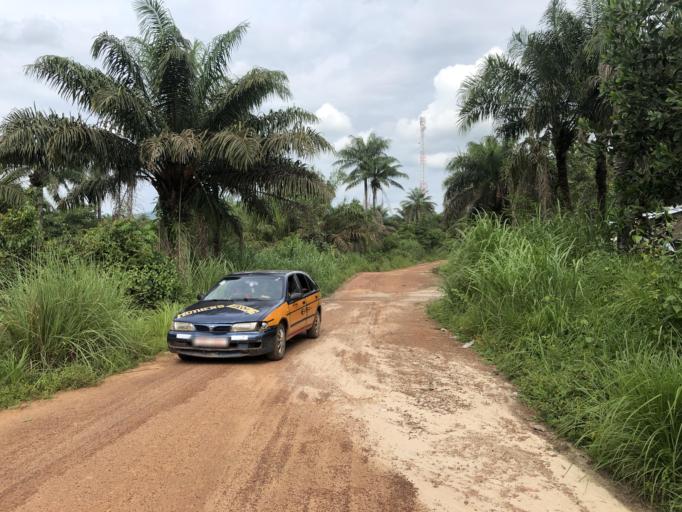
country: SL
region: Northern Province
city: Masaka
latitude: 8.7515
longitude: -11.8447
